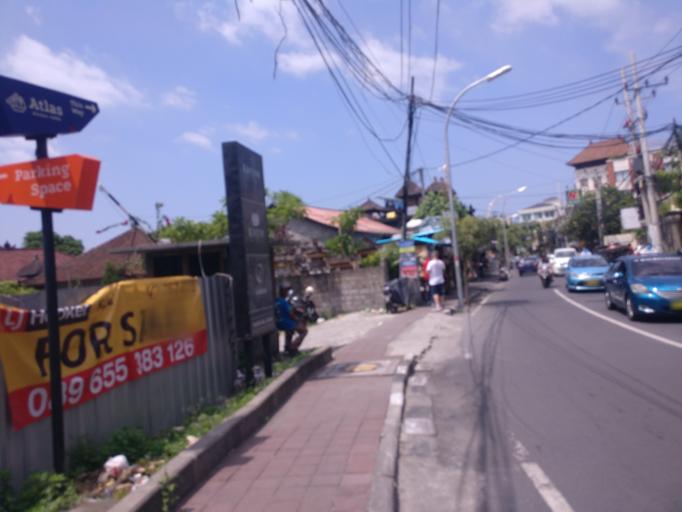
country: ID
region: Bali
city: Kuta
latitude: -8.6764
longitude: 115.1567
